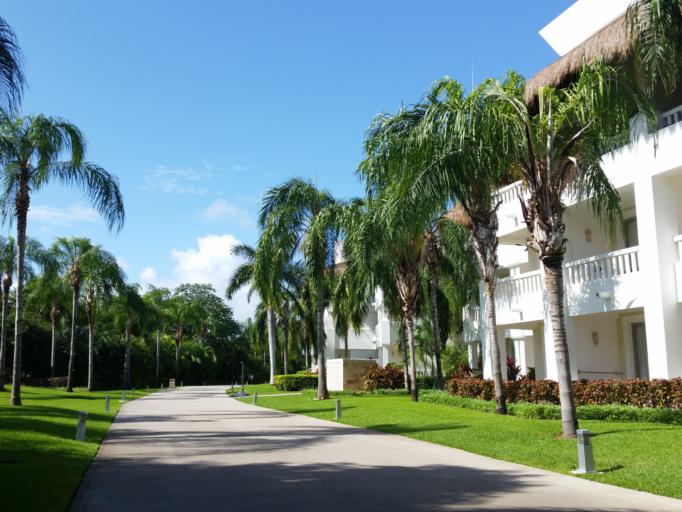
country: MX
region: Quintana Roo
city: Playa del Carmen
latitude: 20.6703
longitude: -87.0331
